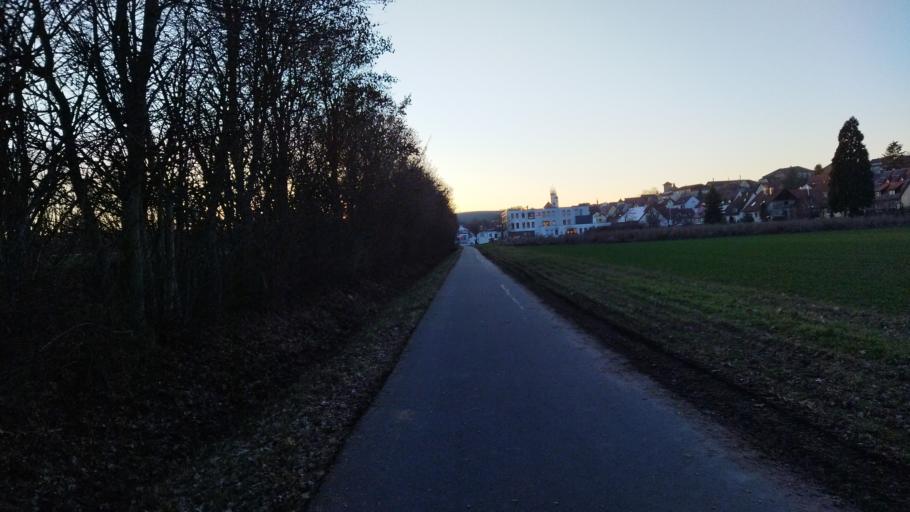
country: DE
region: Bavaria
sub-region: Regierungsbezirk Unterfranken
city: Dettelbach
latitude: 49.8025
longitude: 10.1717
